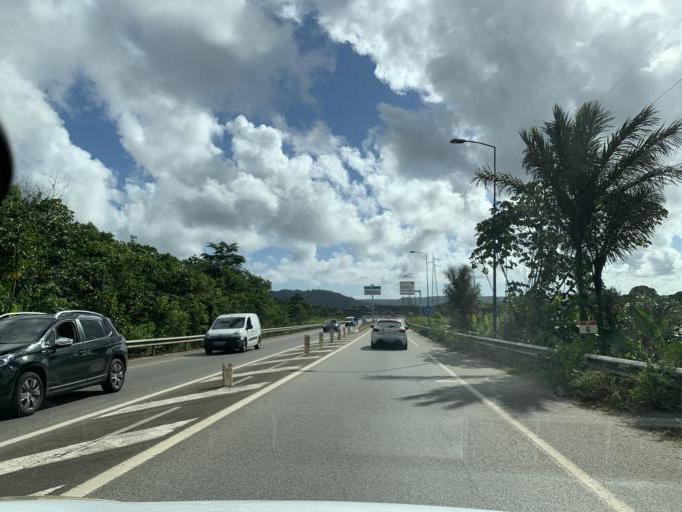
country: GF
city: Macouria
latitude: 4.8913
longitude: -52.3401
